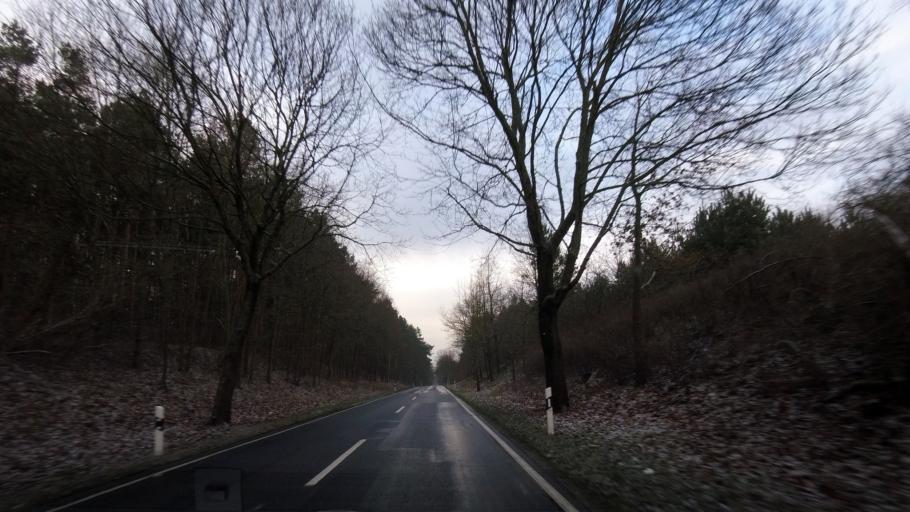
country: DE
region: Brandenburg
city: Treuenbrietzen
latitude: 52.0616
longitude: 12.9411
